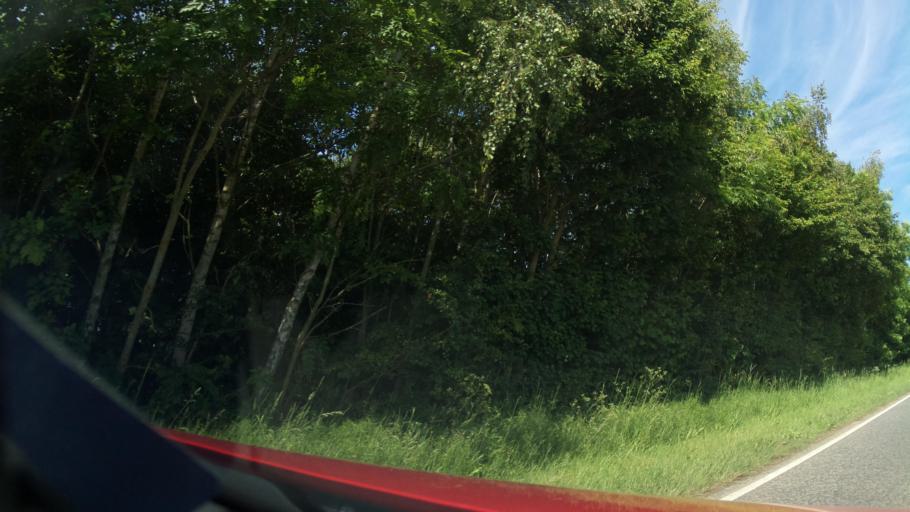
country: GB
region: England
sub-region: Lincolnshire
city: Skellingthorpe
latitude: 53.1667
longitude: -0.6419
